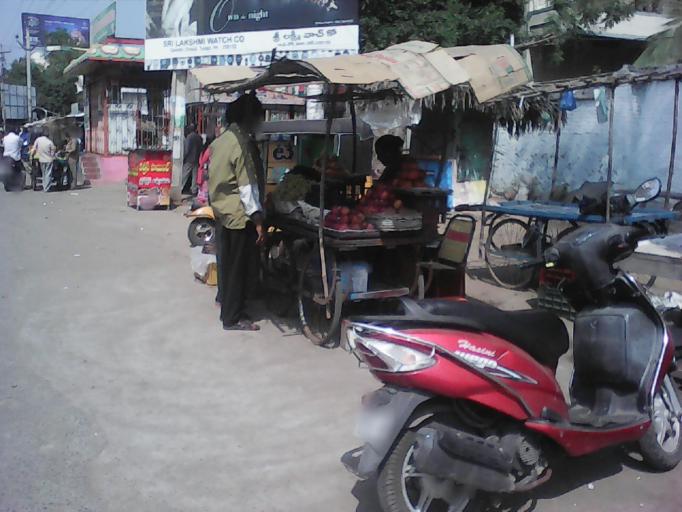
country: IN
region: Andhra Pradesh
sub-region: Guntur
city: Bhattiprolu
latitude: 16.2329
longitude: 80.6506
